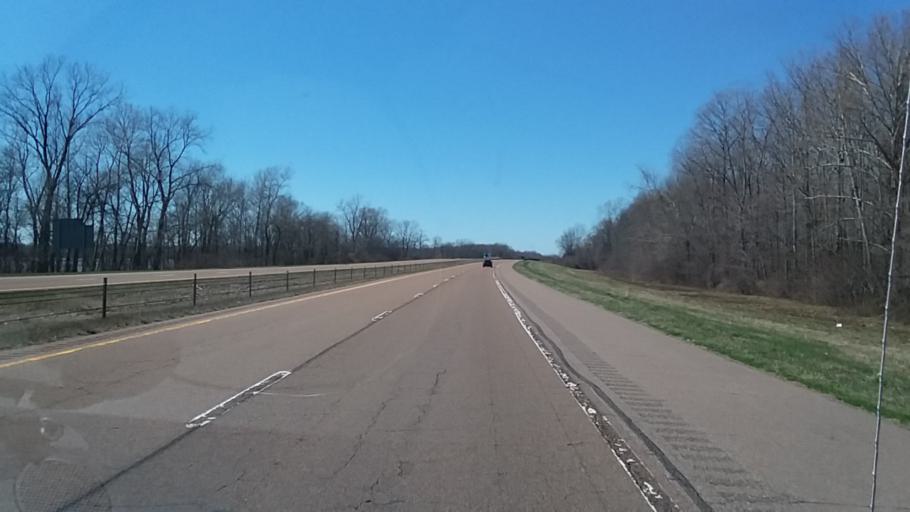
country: US
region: Tennessee
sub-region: Dyer County
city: Dyersburg
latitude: 36.0775
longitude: -89.5126
